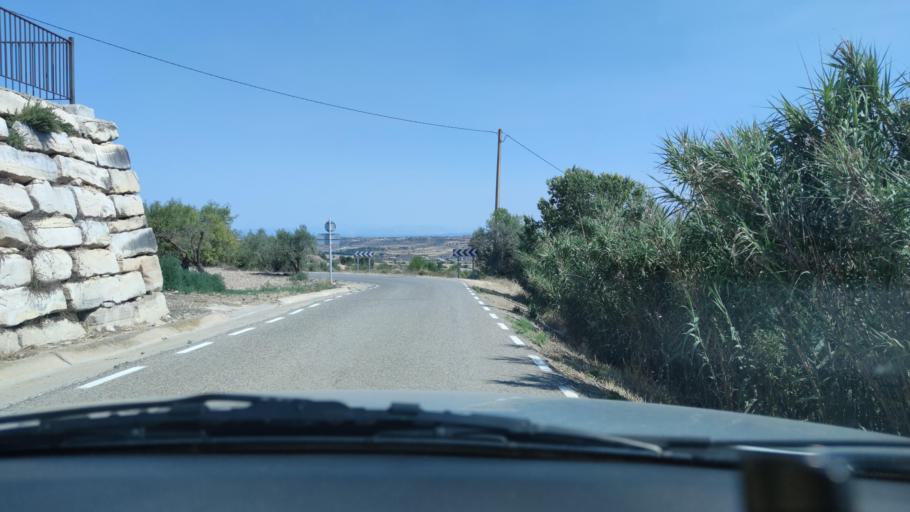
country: ES
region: Catalonia
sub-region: Provincia de Lleida
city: Cervera
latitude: 41.6247
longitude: 1.3206
